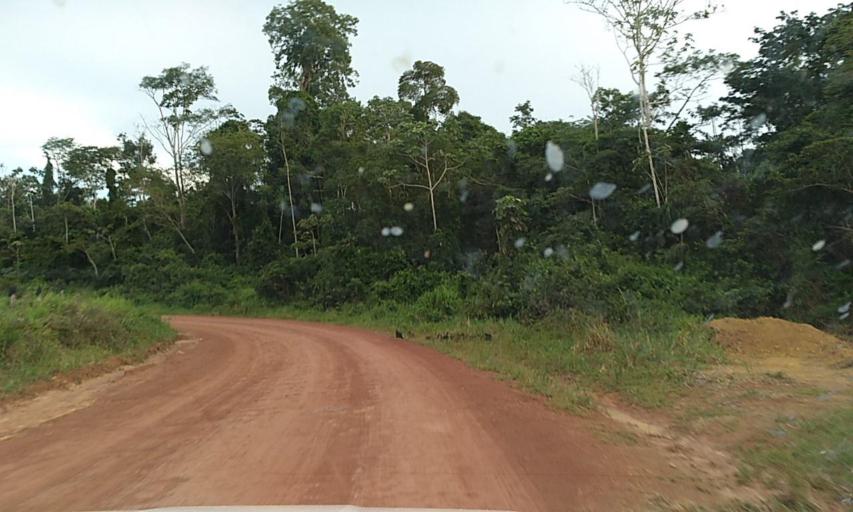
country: BR
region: Para
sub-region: Senador Jose Porfirio
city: Senador Jose Porfirio
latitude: -2.7029
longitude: -51.8188
